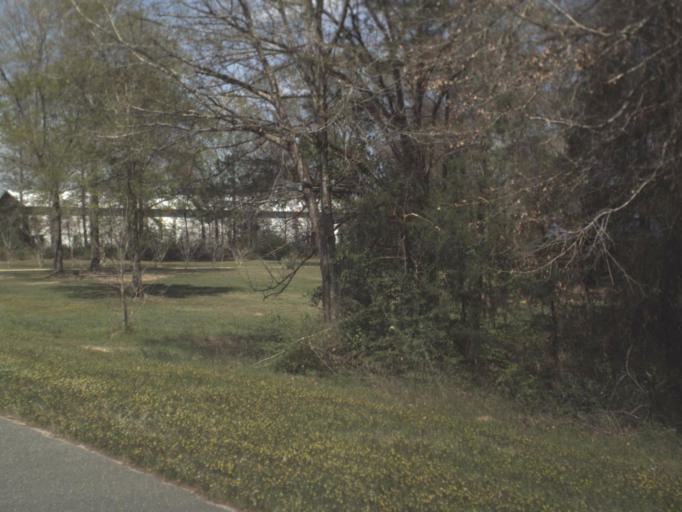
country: US
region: Florida
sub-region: Holmes County
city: Bonifay
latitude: 30.7795
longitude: -85.6371
